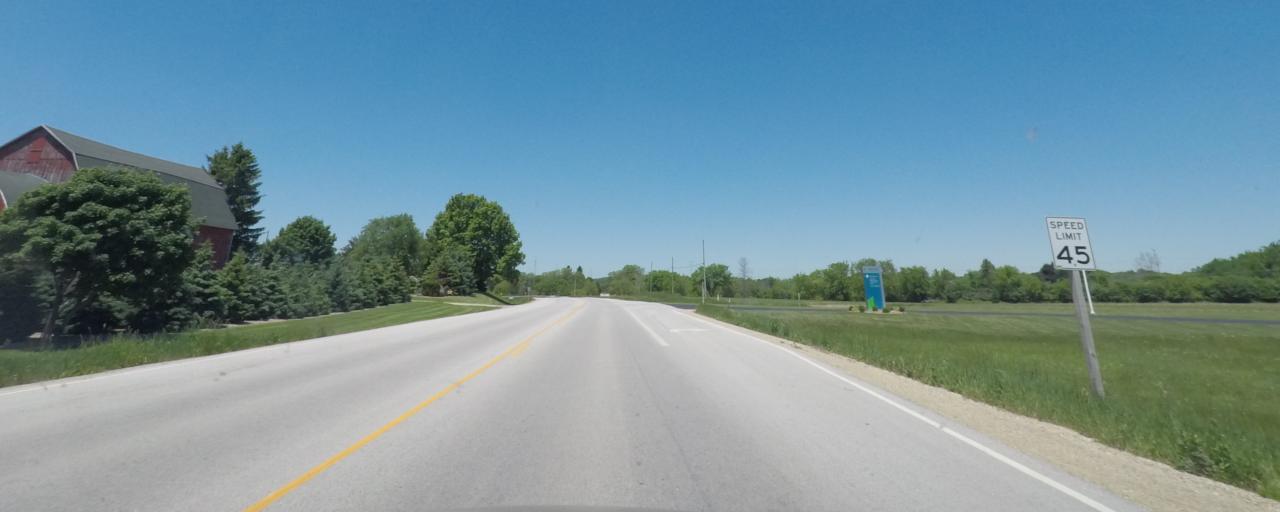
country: US
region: Wisconsin
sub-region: Washington County
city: West Bend
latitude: 43.4499
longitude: -88.1932
